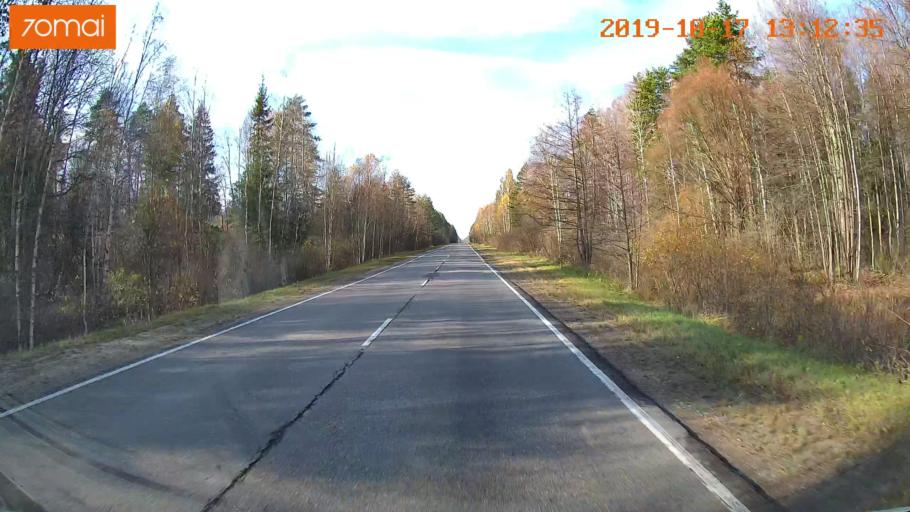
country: RU
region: Rjazan
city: Gus'-Zheleznyy
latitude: 55.0377
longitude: 41.2097
